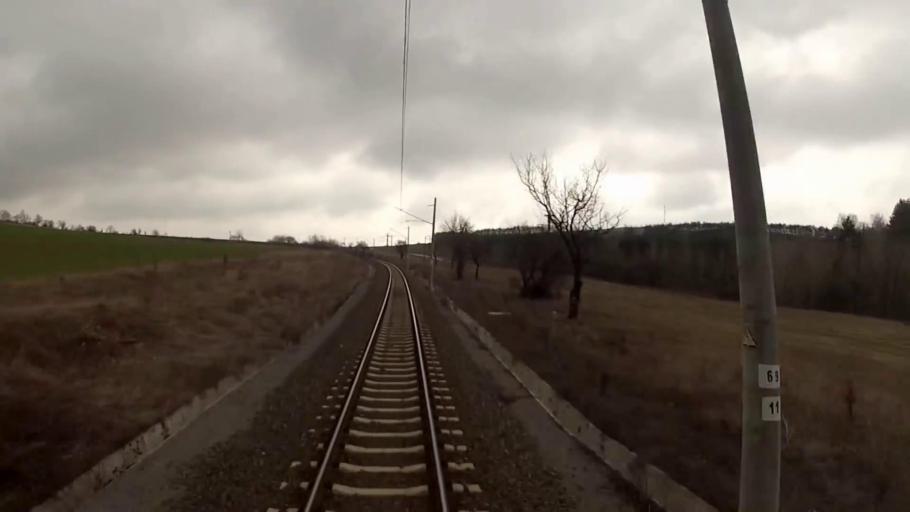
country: BG
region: Sofiya
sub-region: Obshtina Mirkovo
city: Mirkovo
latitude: 42.6936
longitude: 24.0240
